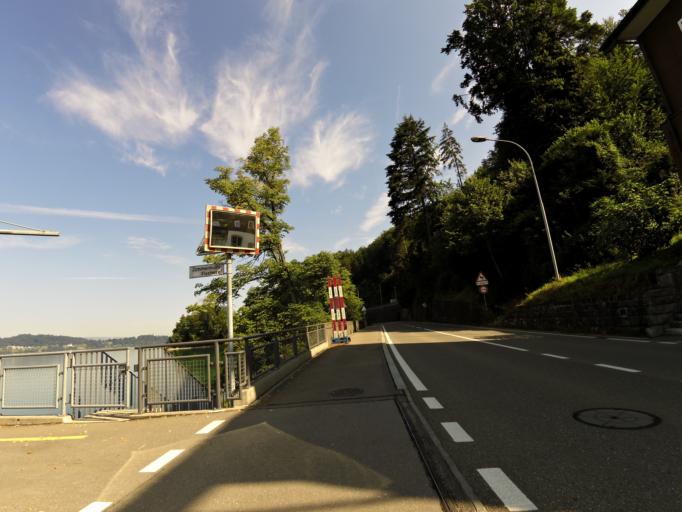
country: CH
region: Zug
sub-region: Zug
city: Walchwil
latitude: 47.1154
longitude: 8.4999
